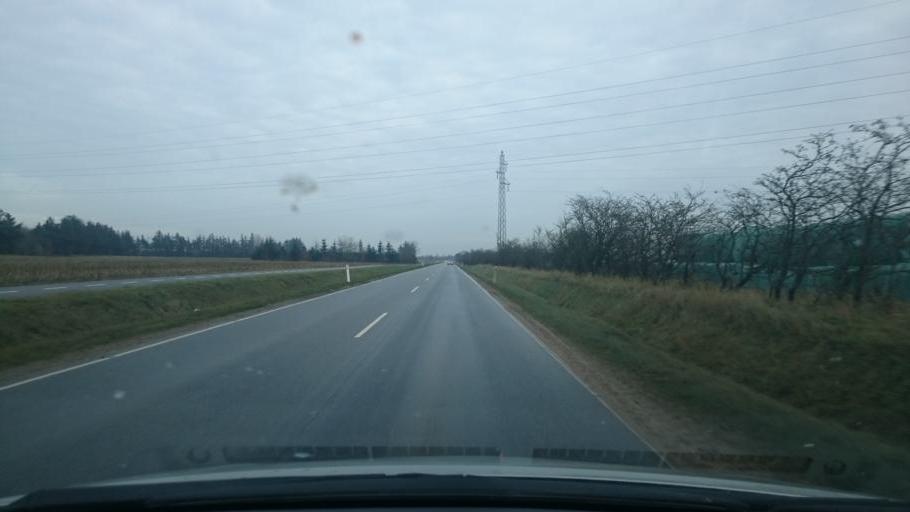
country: DK
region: South Denmark
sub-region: Esbjerg Kommune
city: Ribe
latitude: 55.3337
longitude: 8.8049
